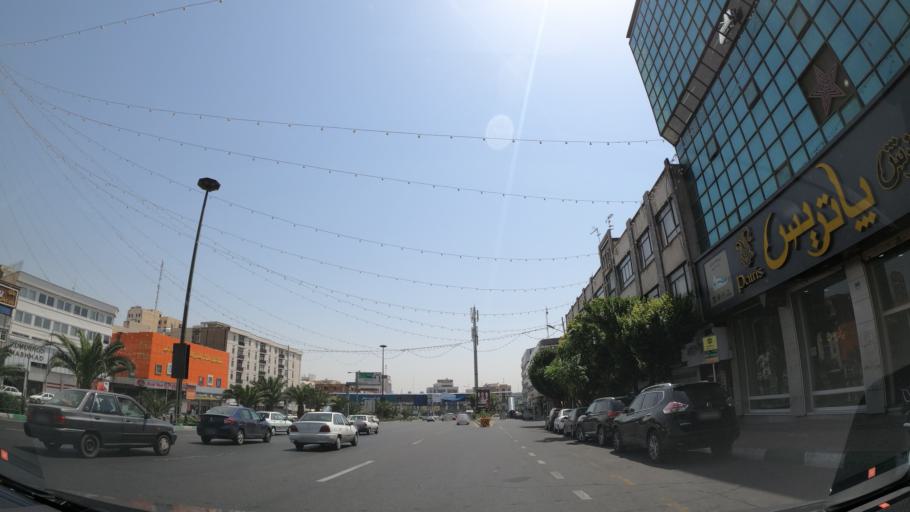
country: IR
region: Tehran
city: Tehran
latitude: 35.7182
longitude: 51.4271
